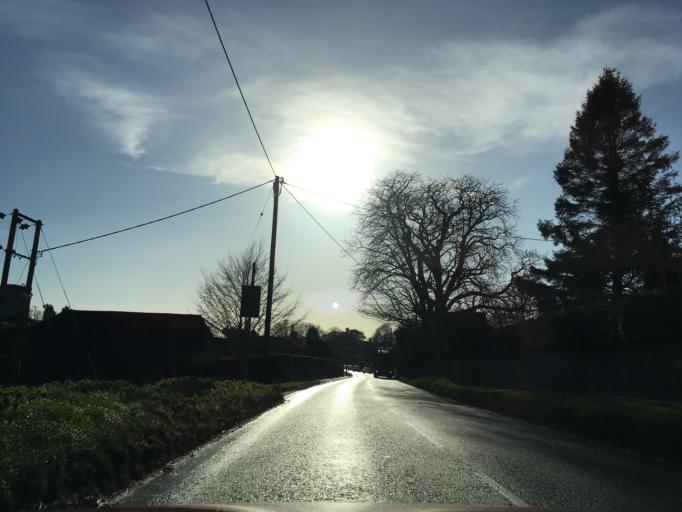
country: GB
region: England
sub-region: Wiltshire
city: Collingbourne Kingston
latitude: 51.2904
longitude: -1.6536
